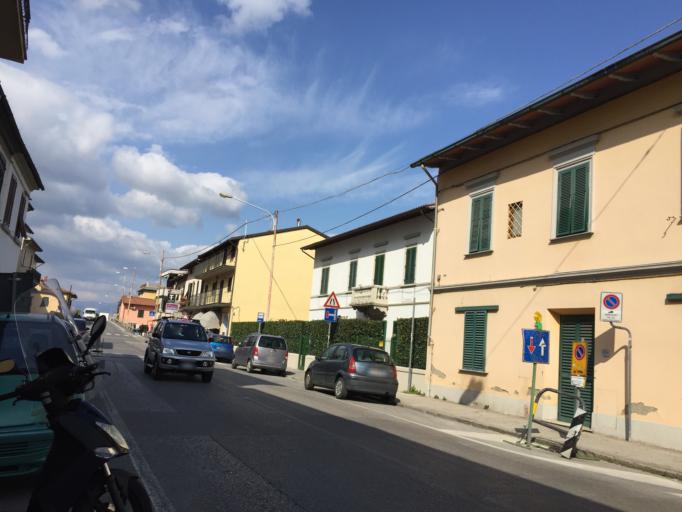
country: IT
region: Tuscany
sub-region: Provincia di Prato
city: Fornacelle
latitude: 43.8959
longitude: 11.0628
